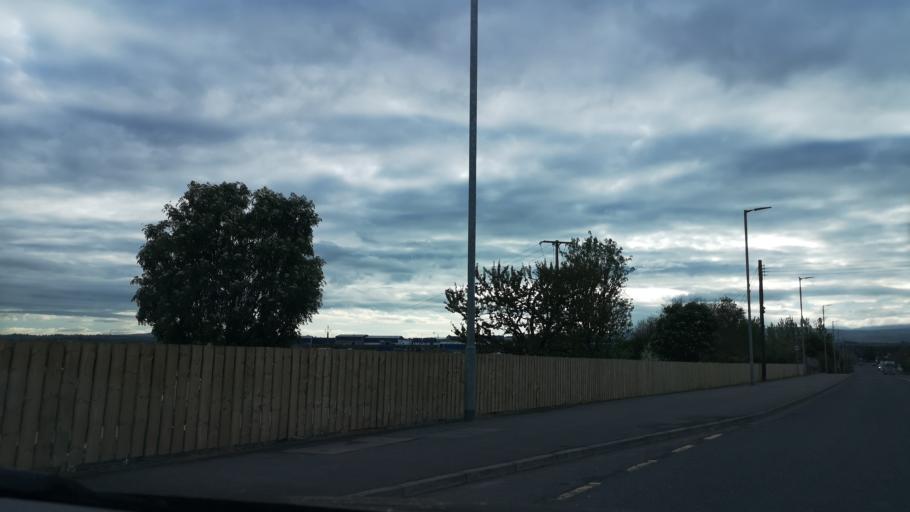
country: GB
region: Northern Ireland
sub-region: Newry and Mourne District
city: Newry
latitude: 54.1871
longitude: -6.3731
